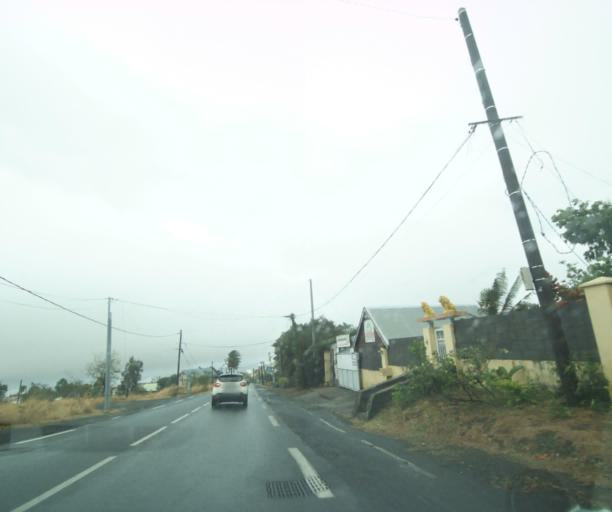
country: RE
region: Reunion
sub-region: Reunion
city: Saint-Paul
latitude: -21.0449
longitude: 55.2586
